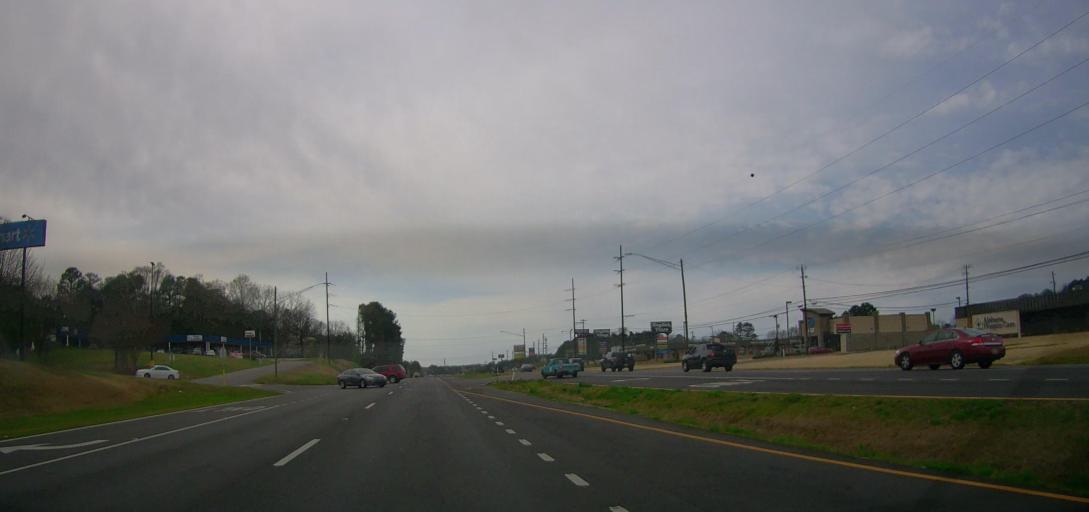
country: US
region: Alabama
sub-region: Walker County
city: Jasper
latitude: 33.8451
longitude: -87.2548
